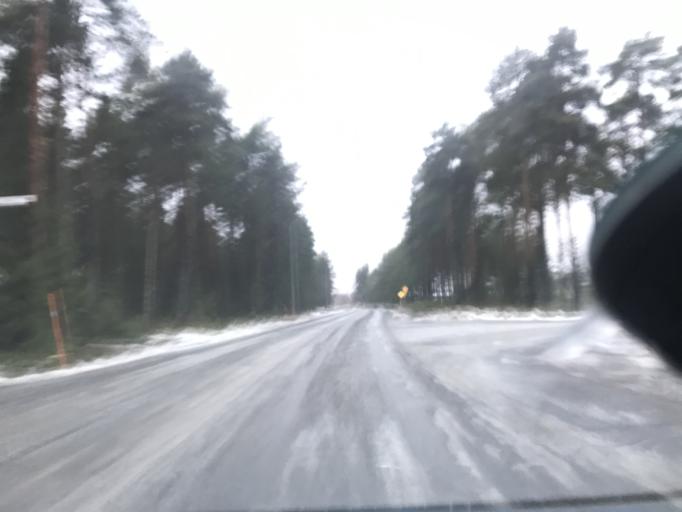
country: SE
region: Norrbotten
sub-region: Lulea Kommun
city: Sodra Sunderbyn
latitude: 65.6509
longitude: 21.9551
